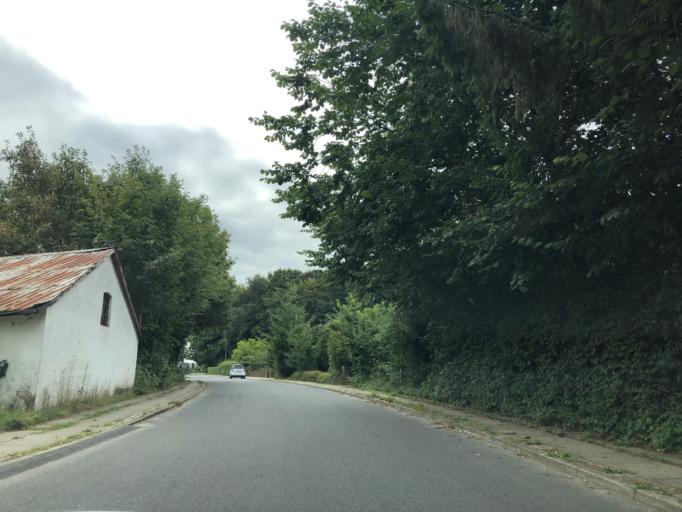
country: DK
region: North Denmark
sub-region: Alborg Kommune
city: Nibe
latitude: 56.8504
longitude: 9.6968
